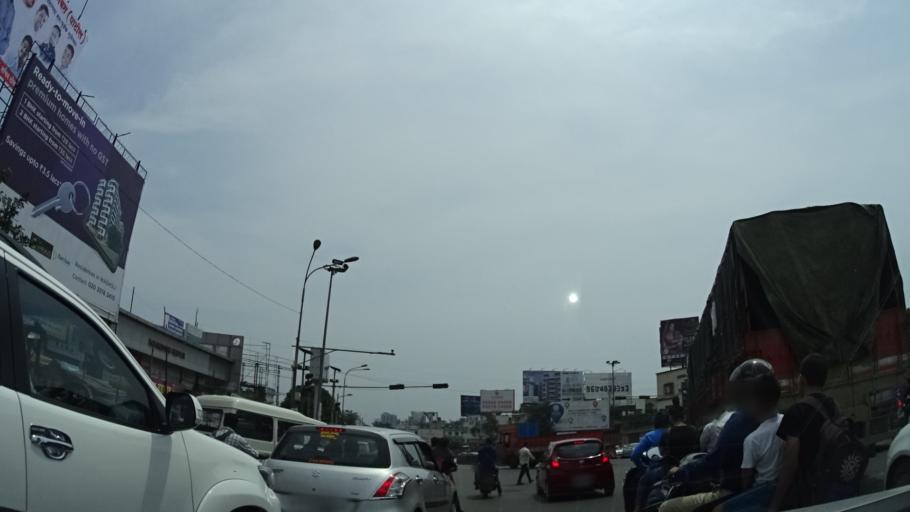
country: IN
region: Maharashtra
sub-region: Pune Division
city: Lohogaon
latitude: 18.5624
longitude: 73.9384
